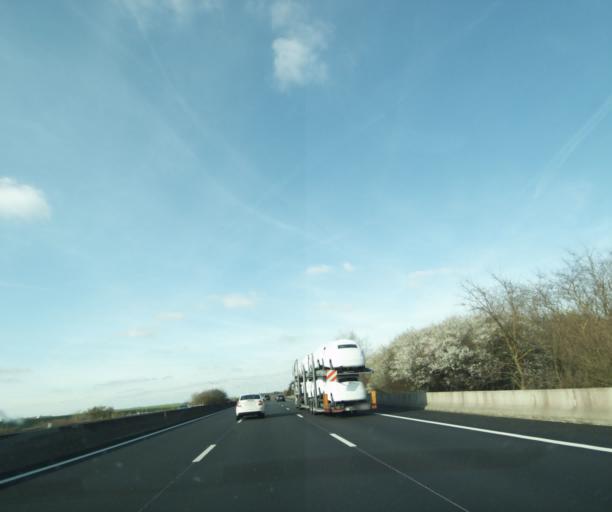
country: FR
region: Centre
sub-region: Departement d'Eure-et-Loir
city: Janville
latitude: 48.2473
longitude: 1.8515
